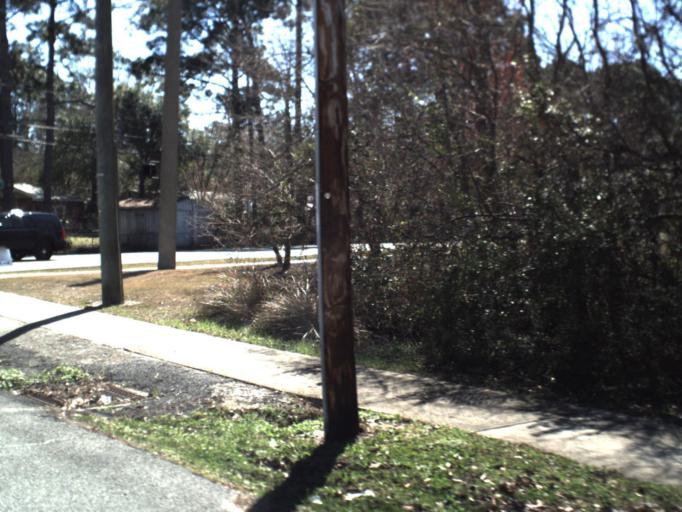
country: US
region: Florida
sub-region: Bay County
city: Pretty Bayou
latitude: 30.1884
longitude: -85.6761
